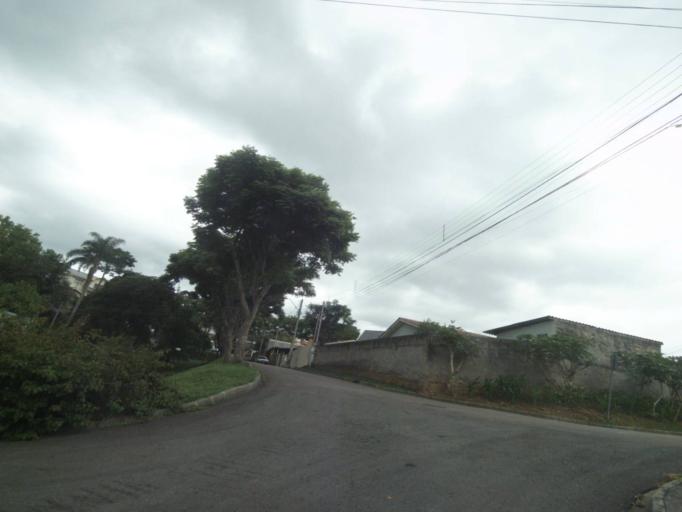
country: BR
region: Parana
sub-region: Curitiba
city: Curitiba
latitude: -25.3843
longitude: -49.2885
